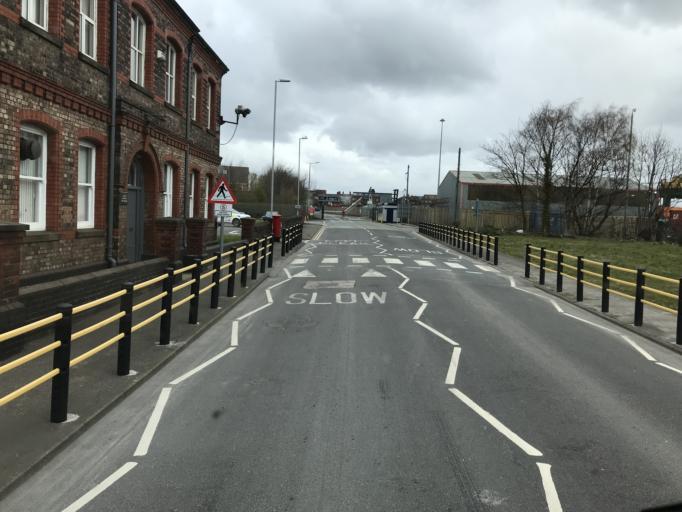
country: GB
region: England
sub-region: Metropolitan Borough of Wirral
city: Bromborough
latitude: 53.3527
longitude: -2.9061
